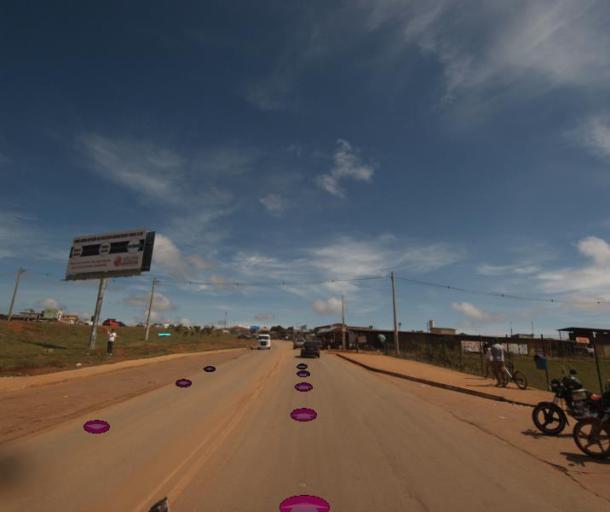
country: BR
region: Federal District
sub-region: Brasilia
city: Brasilia
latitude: -15.7362
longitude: -48.2749
